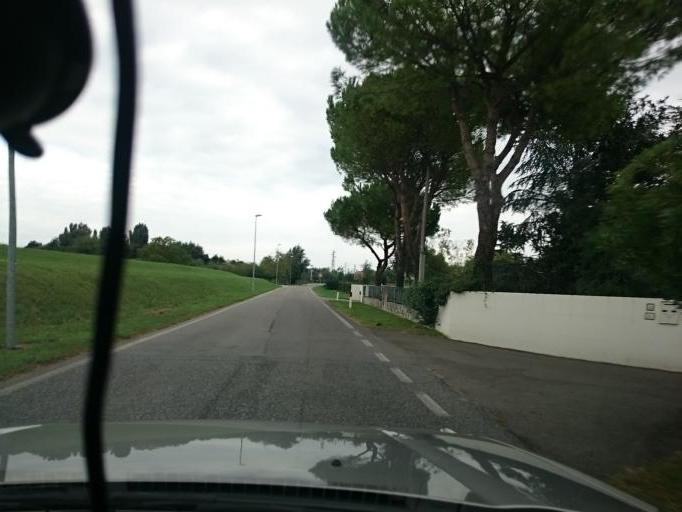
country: IT
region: Veneto
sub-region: Provincia di Padova
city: Saccolongo
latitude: 45.4193
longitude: 11.7496
